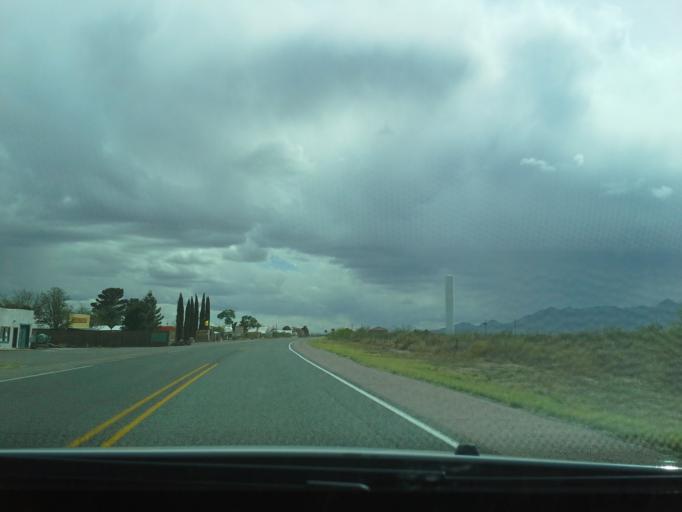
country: US
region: New Mexico
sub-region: Hidalgo County
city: Lordsburg
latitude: 31.8397
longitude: -109.0291
